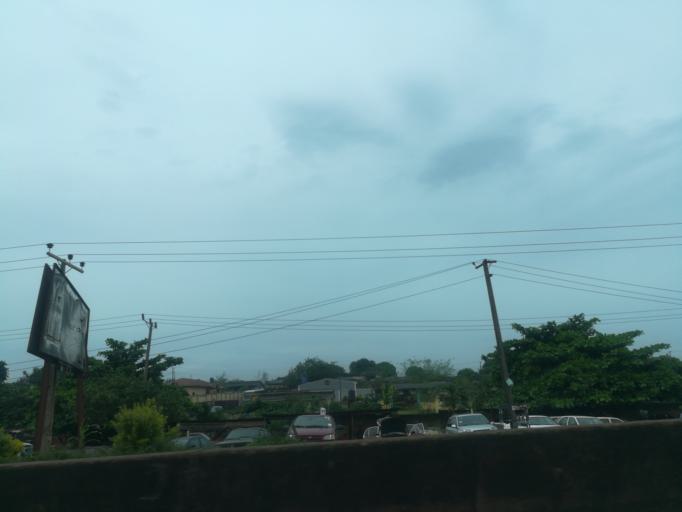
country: NG
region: Oyo
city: Ibadan
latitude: 7.3947
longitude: 3.9602
